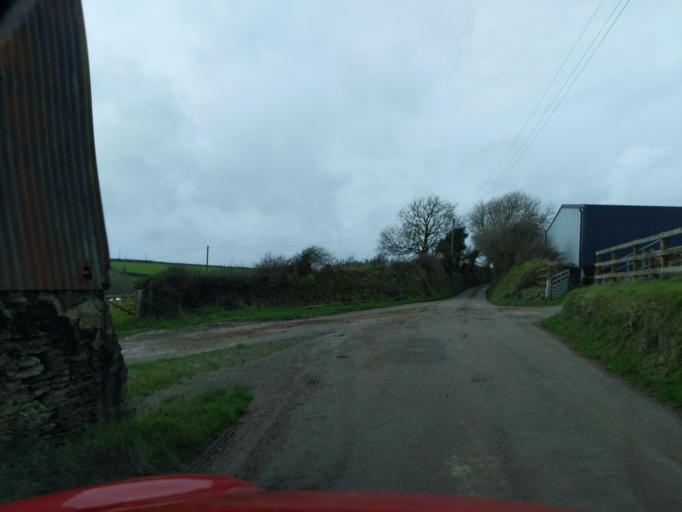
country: GB
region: England
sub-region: Cornwall
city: Duloe
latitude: 50.3487
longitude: -4.5441
